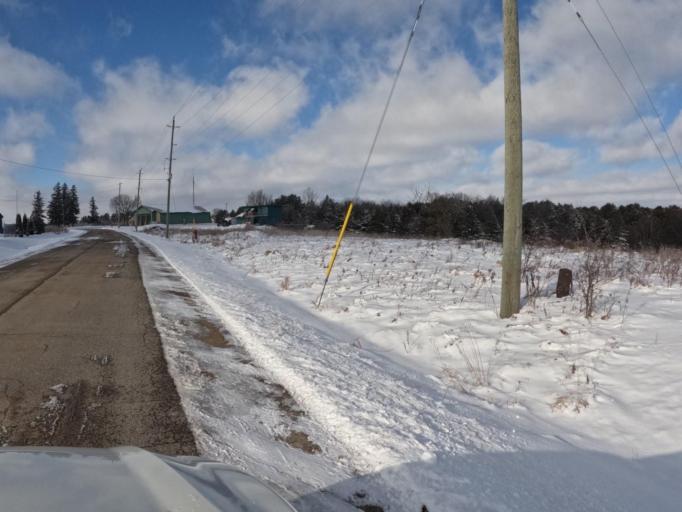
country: CA
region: Ontario
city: Orangeville
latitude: 43.8876
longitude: -80.3097
